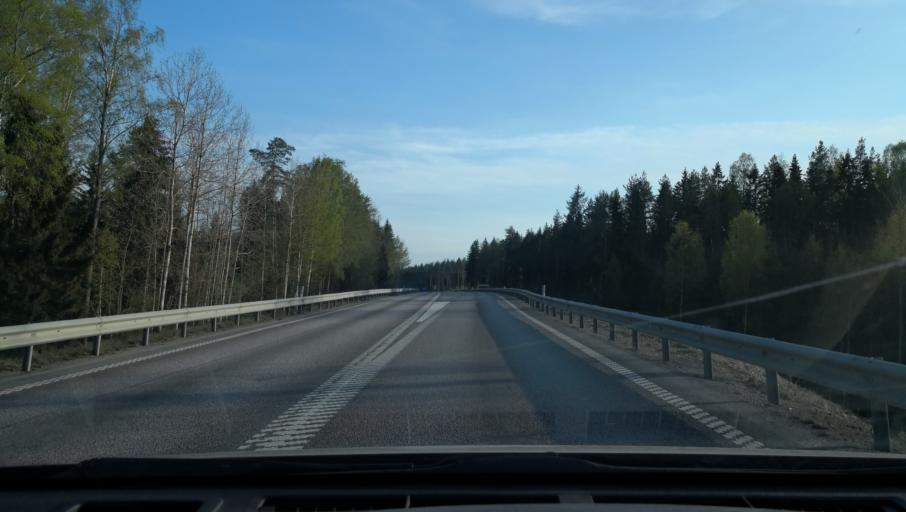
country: SE
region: Uppsala
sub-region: Heby Kommun
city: Heby
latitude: 59.9473
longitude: 16.8325
